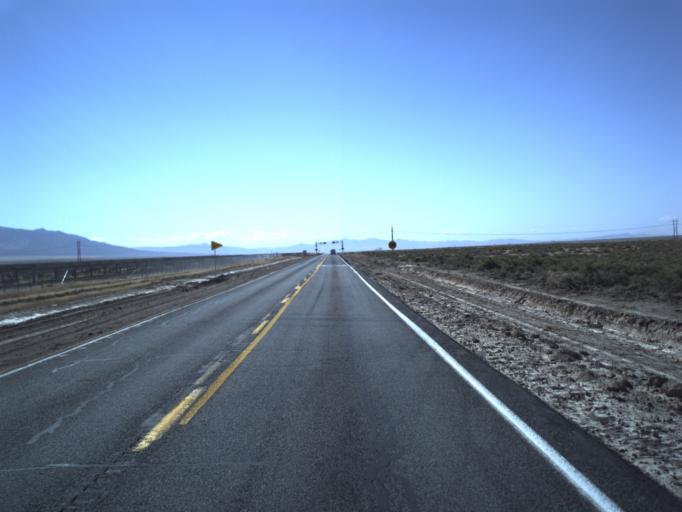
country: US
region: Utah
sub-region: Beaver County
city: Milford
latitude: 38.4985
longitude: -112.9912
